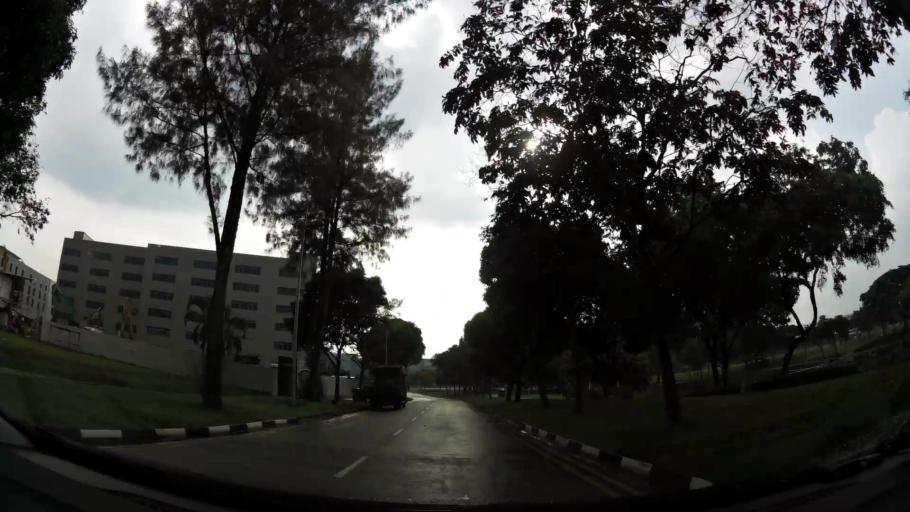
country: SG
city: Singapore
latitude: 1.3387
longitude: 103.9681
